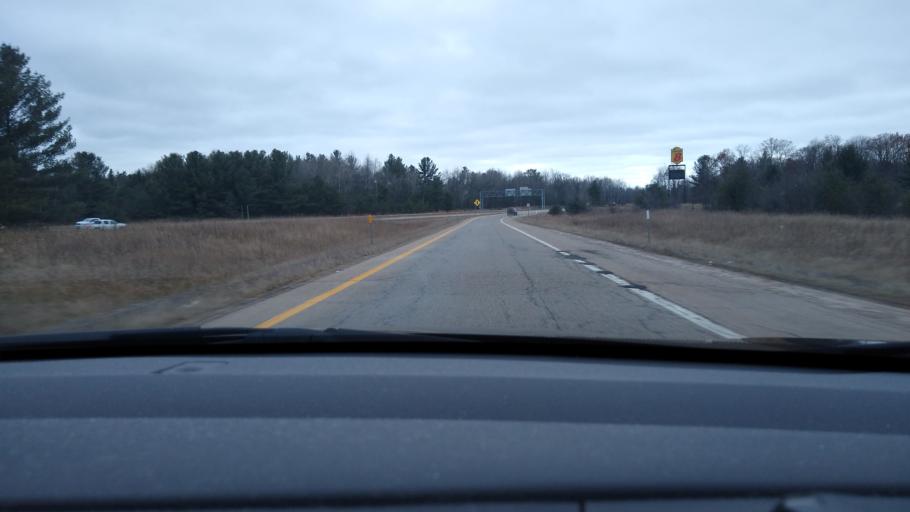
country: US
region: Michigan
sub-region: Roscommon County
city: Houghton Lake
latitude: 44.3379
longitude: -84.8061
